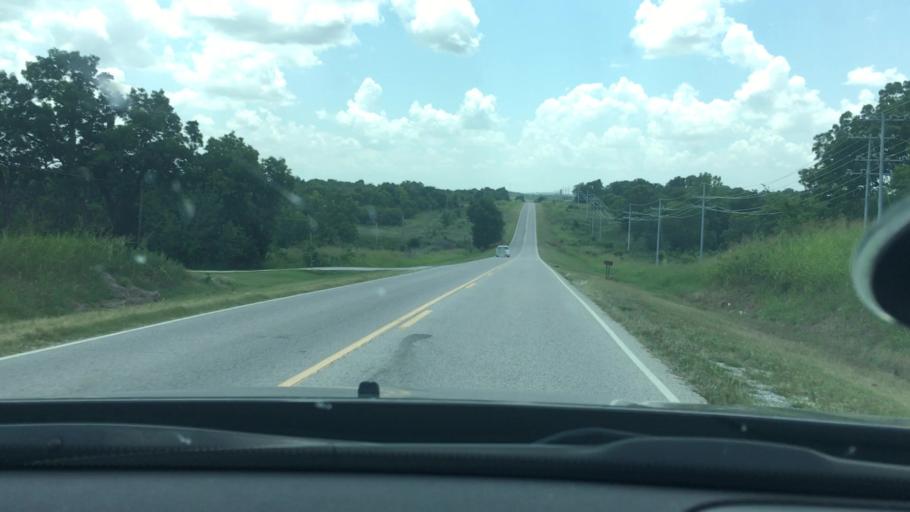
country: US
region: Oklahoma
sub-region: Pontotoc County
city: Ada
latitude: 34.6299
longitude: -96.6349
